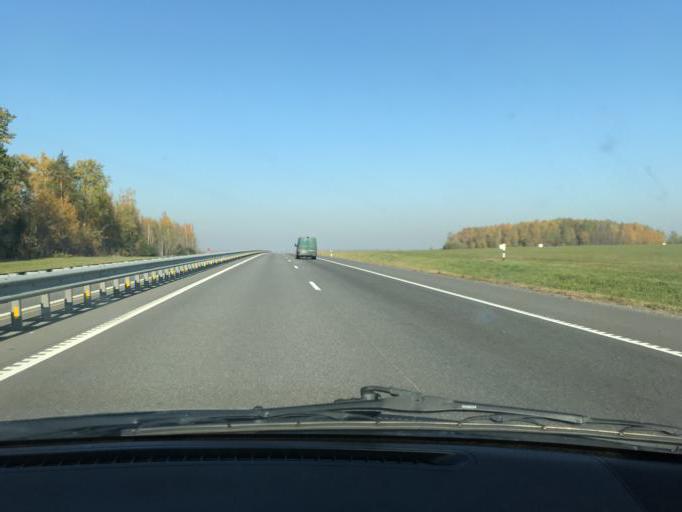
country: BY
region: Minsk
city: Slutsk
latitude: 53.2019
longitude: 27.5510
